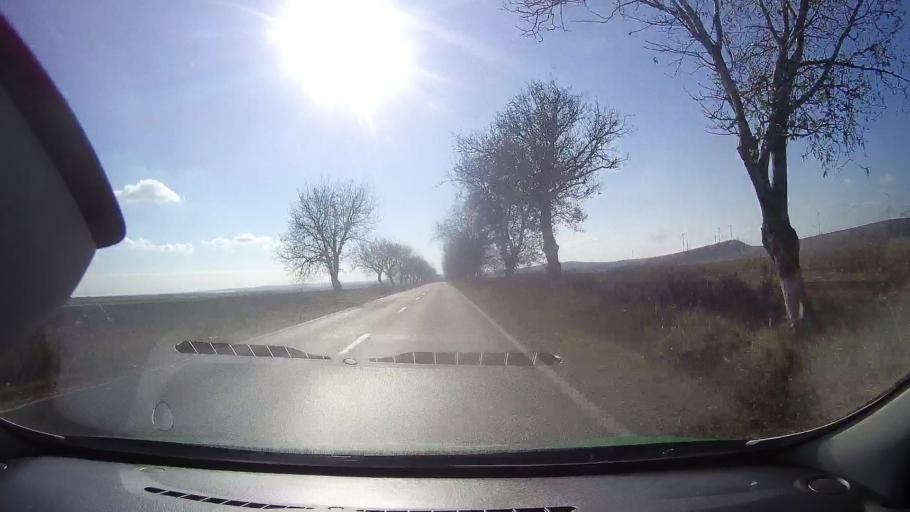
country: RO
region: Tulcea
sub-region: Comuna Ceamurlia de Jos
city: Ceamurlia de Jos
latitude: 44.7900
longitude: 28.6898
